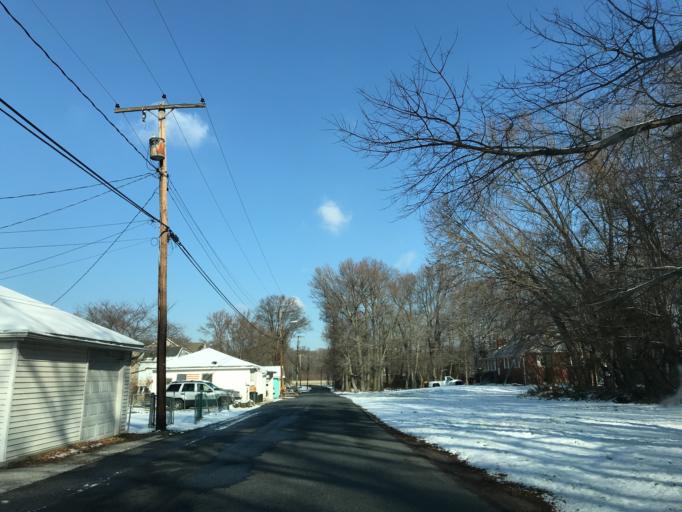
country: US
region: Maryland
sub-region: Baltimore County
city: Bowleys Quarters
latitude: 39.3075
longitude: -76.3797
